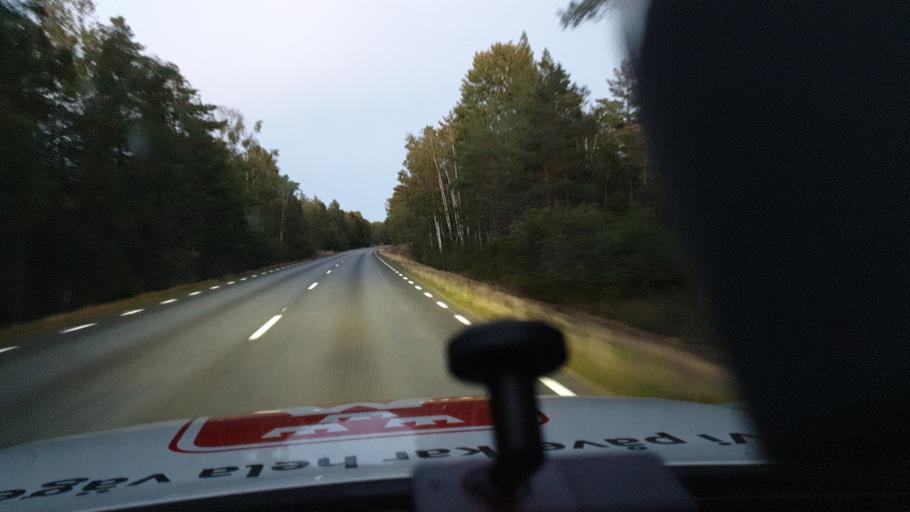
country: SE
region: Kalmar
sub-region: Oskarshamns Kommun
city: Paskallavik
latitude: 57.1838
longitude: 16.3925
